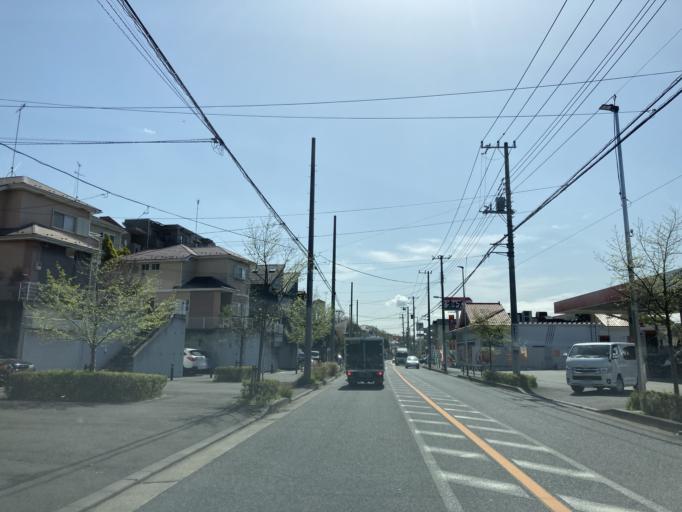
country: JP
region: Tokyo
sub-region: Machida-shi
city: Machida
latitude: 35.5996
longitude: 139.4856
